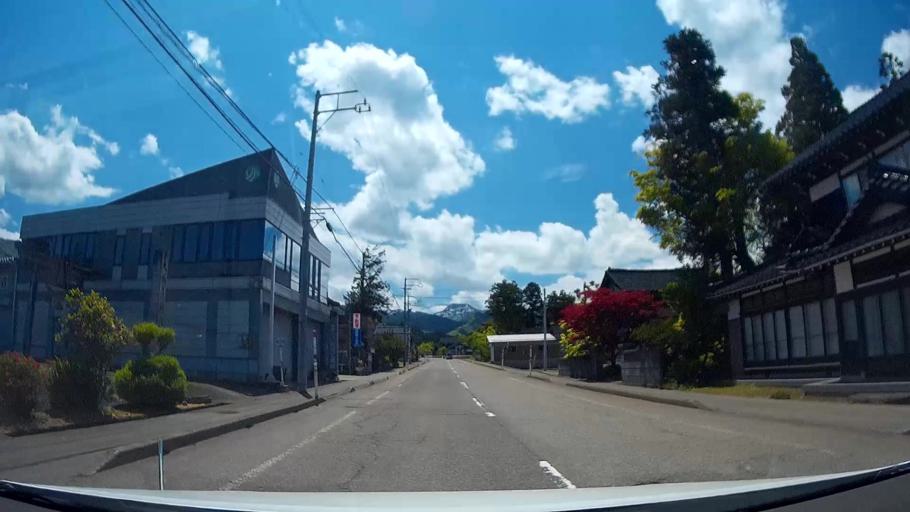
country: JP
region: Toyama
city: Fukumitsu
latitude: 36.4948
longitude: 136.8957
